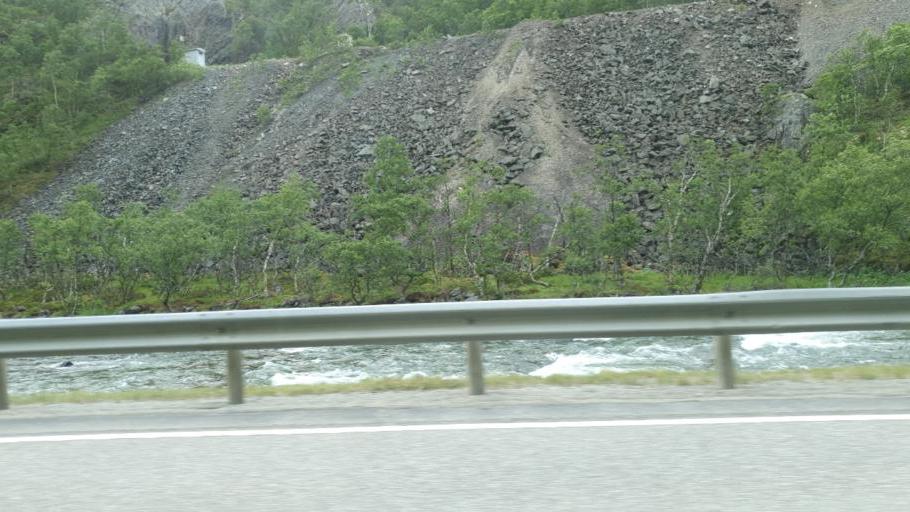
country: NO
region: Sor-Trondelag
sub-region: Oppdal
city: Oppdal
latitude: 62.3392
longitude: 9.6206
